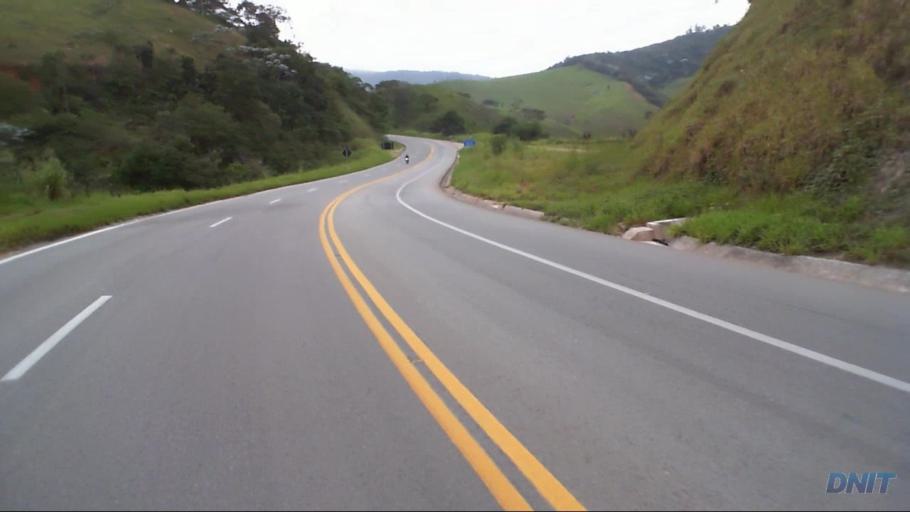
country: BR
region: Minas Gerais
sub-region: Nova Era
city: Nova Era
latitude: -19.6693
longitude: -42.9695
